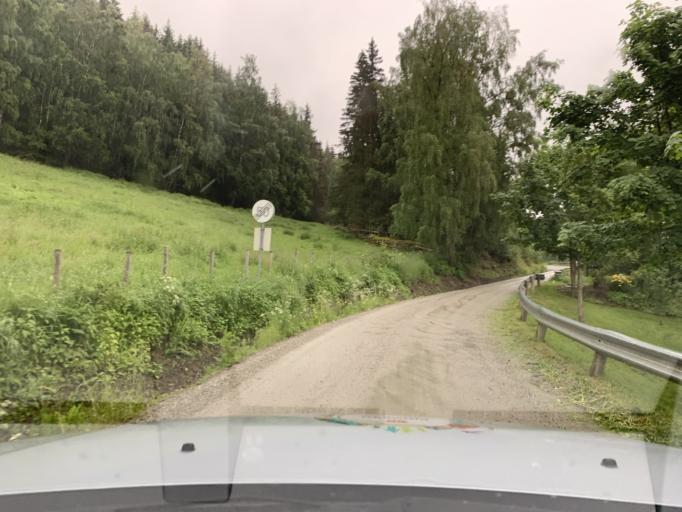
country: NO
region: Oppland
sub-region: Oyer
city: Tretten
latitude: 61.3919
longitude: 10.2479
